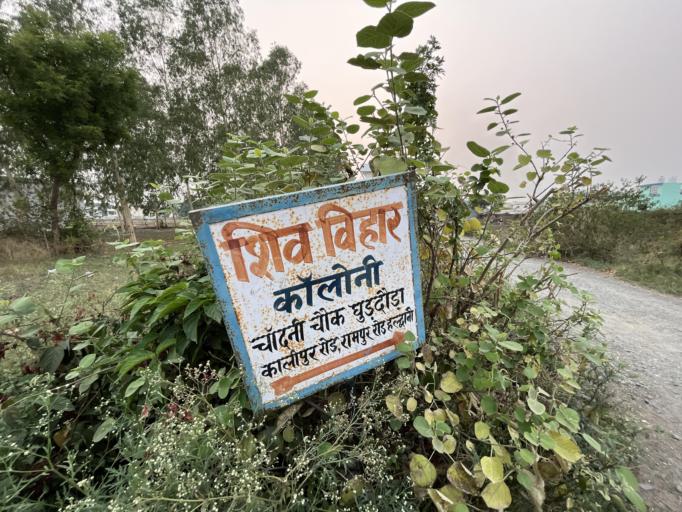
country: IN
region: Uttarakhand
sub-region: Naini Tal
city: Haldwani
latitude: 29.1687
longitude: 79.4811
